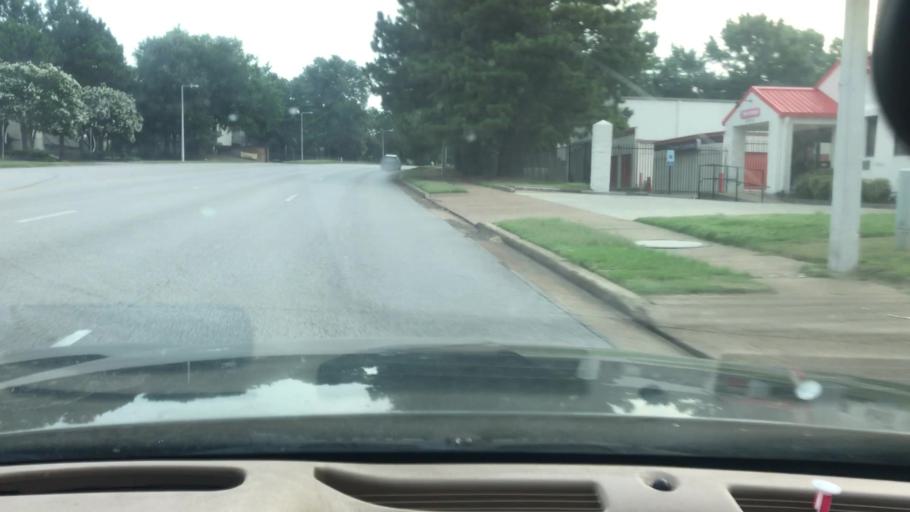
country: US
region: Tennessee
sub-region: Shelby County
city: Bartlett
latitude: 35.1834
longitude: -89.8711
